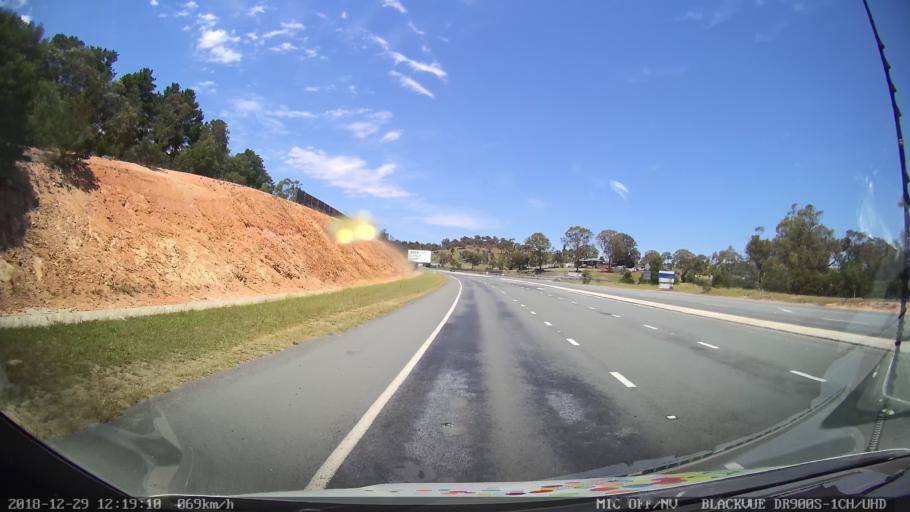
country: AU
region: New South Wales
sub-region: Queanbeyan
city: Queanbeyan
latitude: -35.3910
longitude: 149.2339
